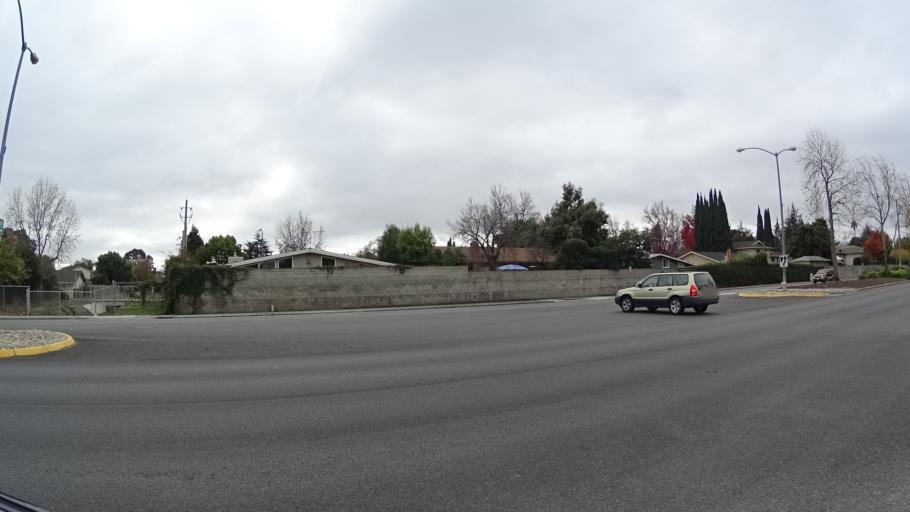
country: US
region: California
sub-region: Santa Clara County
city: Sunnyvale
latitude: 37.3523
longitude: -122.0234
